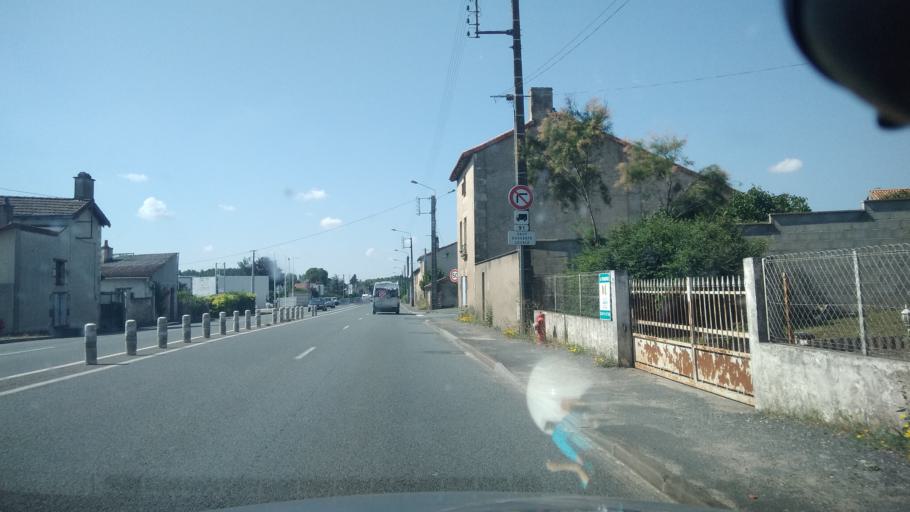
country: FR
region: Poitou-Charentes
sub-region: Departement de la Vienne
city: Chasseneuil-du-Poitou
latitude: 46.6436
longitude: 0.3608
